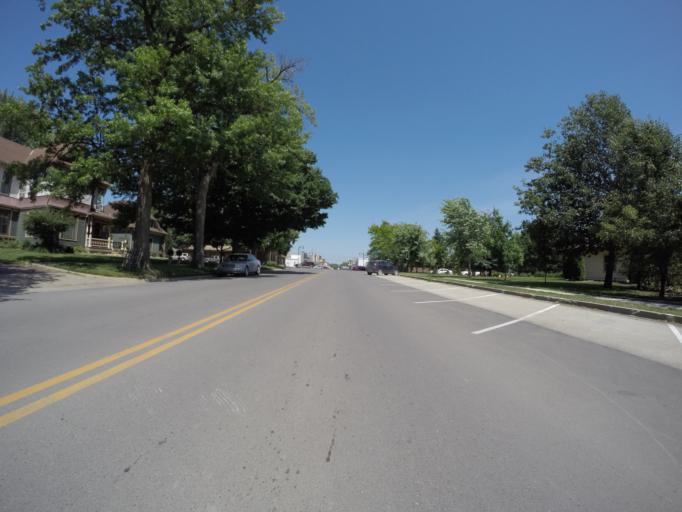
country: US
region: Kansas
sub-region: Nemaha County
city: Sabetha
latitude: 39.9034
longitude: -95.8054
